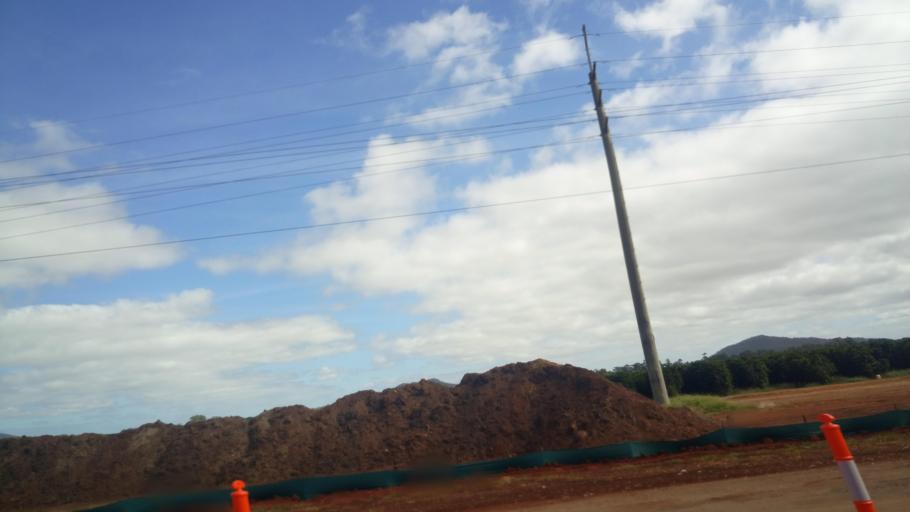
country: AU
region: Queensland
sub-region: Tablelands
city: Mareeba
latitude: -17.1171
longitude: 145.4278
